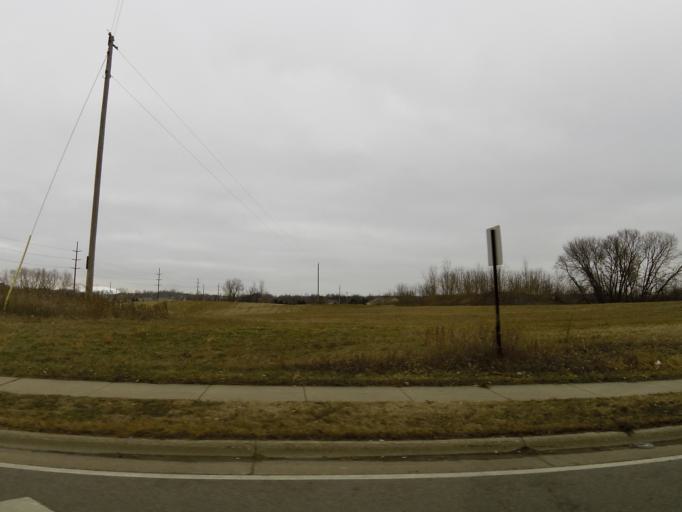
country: US
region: Minnesota
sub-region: Scott County
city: Savage
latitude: 44.7467
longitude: -93.3578
